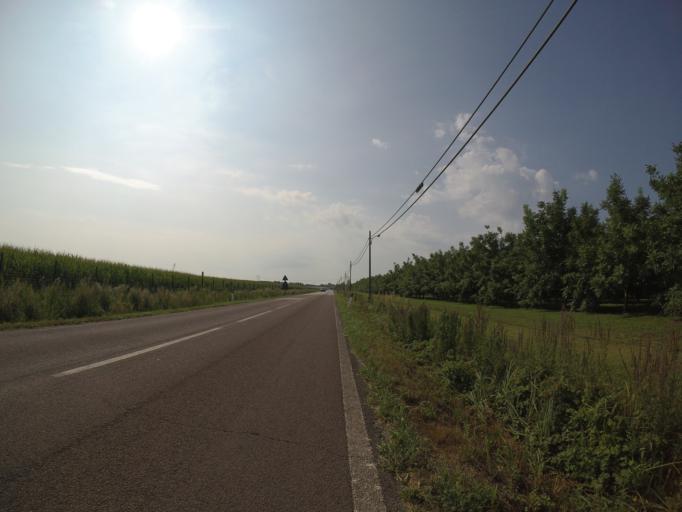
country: IT
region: Friuli Venezia Giulia
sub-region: Provincia di Udine
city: Pocenia
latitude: 45.8345
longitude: 13.0780
